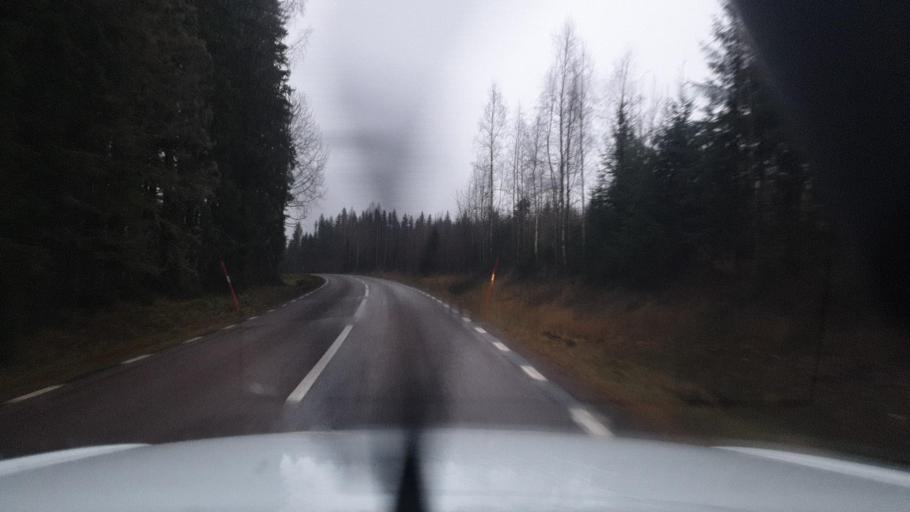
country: SE
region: Vaermland
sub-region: Sunne Kommun
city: Sunne
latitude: 59.9079
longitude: 12.9055
